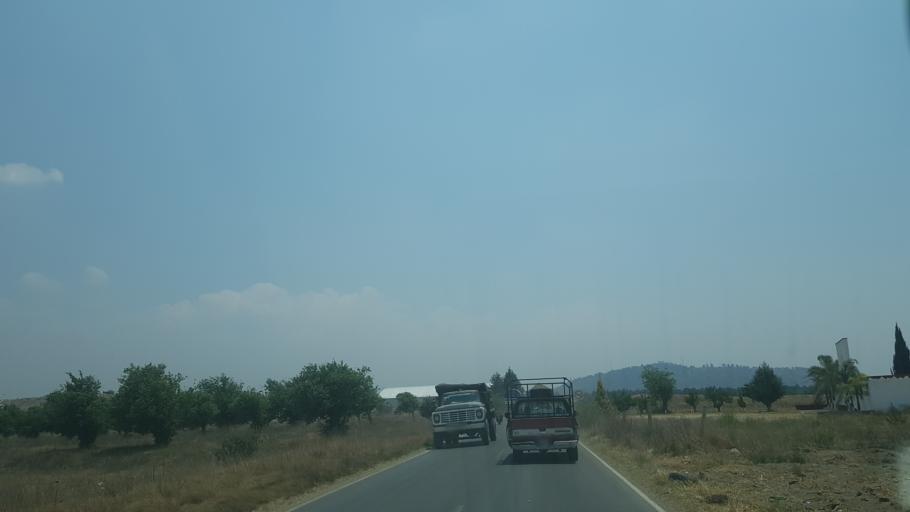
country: MX
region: Puebla
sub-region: San Jeronimo Tecuanipan
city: San Miguel Papaxtla
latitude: 19.0907
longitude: -98.3854
